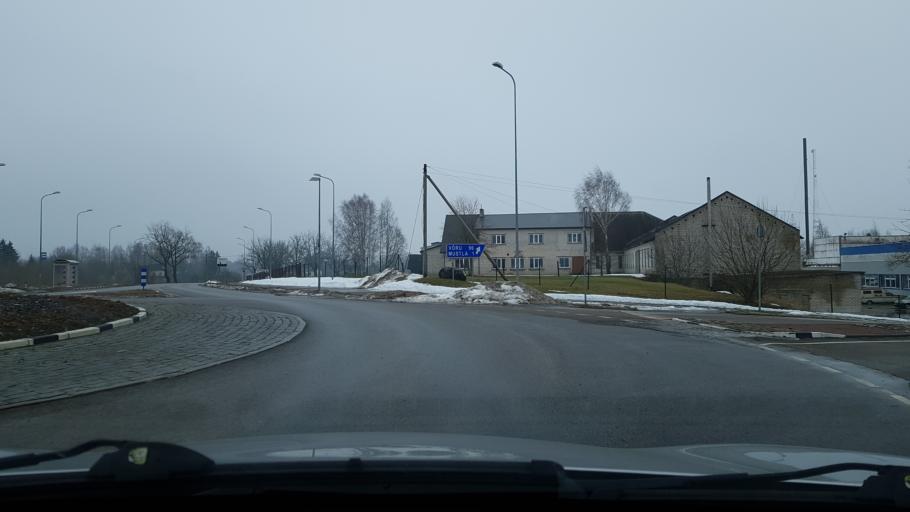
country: EE
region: Viljandimaa
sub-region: Viiratsi vald
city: Viiratsi
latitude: 58.2446
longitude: 25.8533
